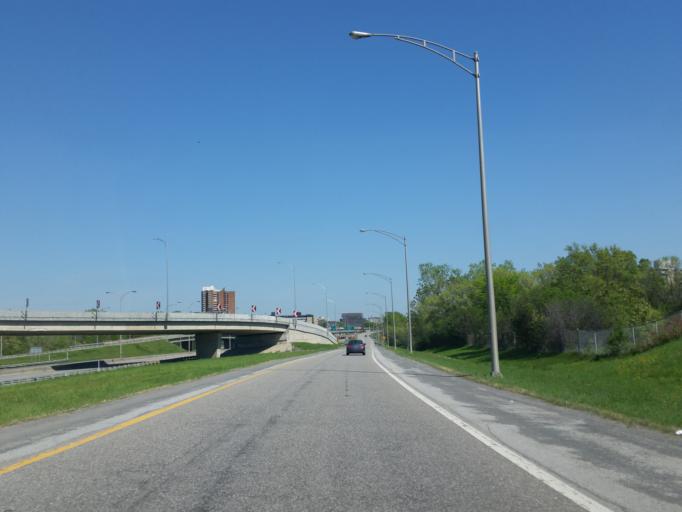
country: CA
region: Ontario
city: Ottawa
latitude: 45.4406
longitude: -75.7212
